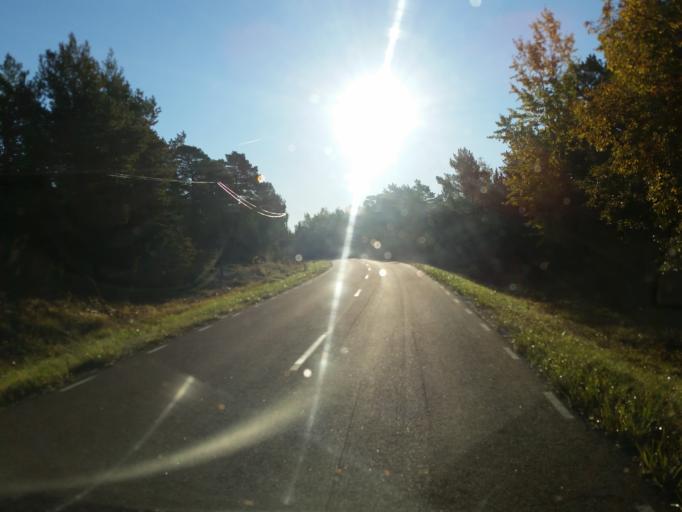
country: AX
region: Alands skaergard
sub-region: Vardoe
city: Vardoe
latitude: 60.2289
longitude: 20.3972
